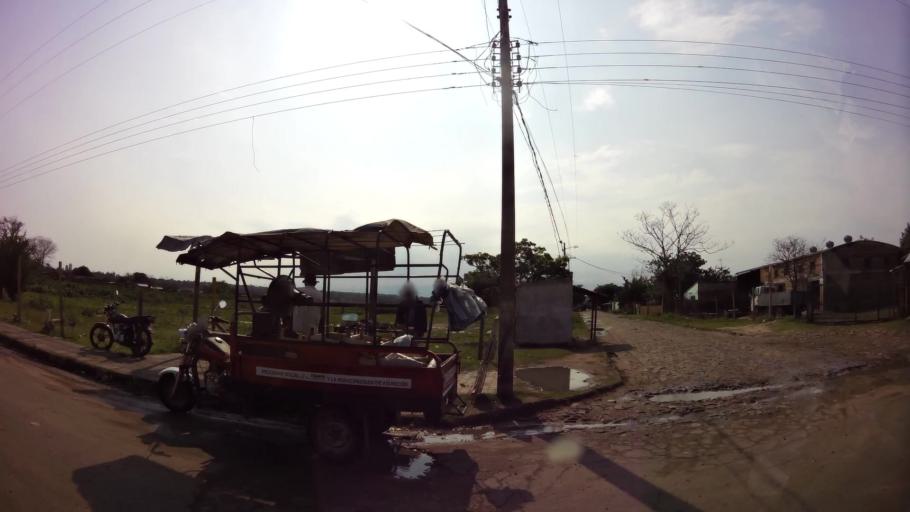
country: PY
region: Asuncion
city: Asuncion
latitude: -25.3123
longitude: -57.6675
